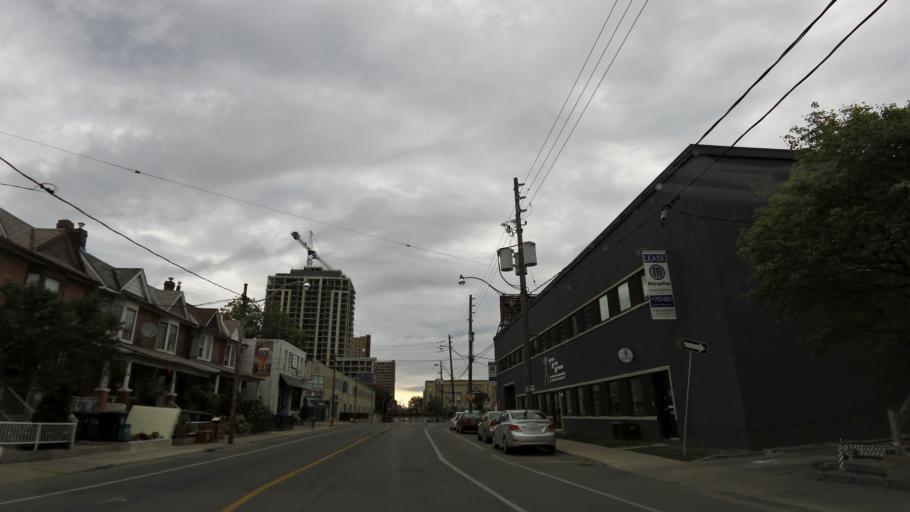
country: CA
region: Ontario
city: Toronto
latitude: 43.6658
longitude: -79.4509
